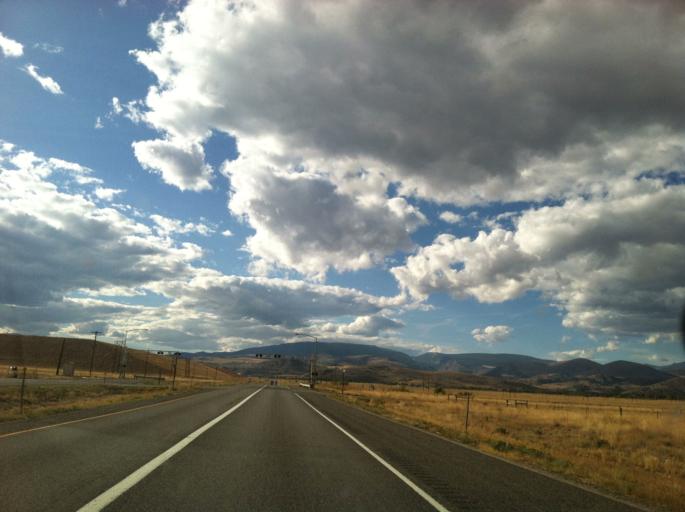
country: US
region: Montana
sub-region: Deer Lodge County
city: Anaconda
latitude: 46.1165
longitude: -112.8695
